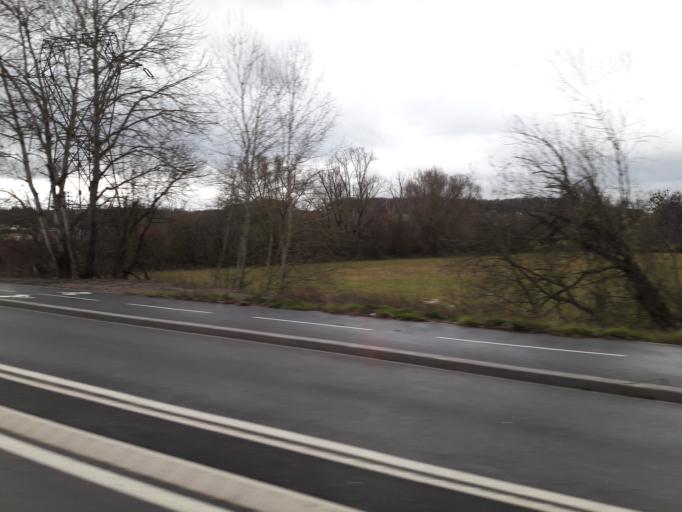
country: FR
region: Franche-Comte
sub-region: Territoire de Belfort
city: Joncherey
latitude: 47.5216
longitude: 7.0017
